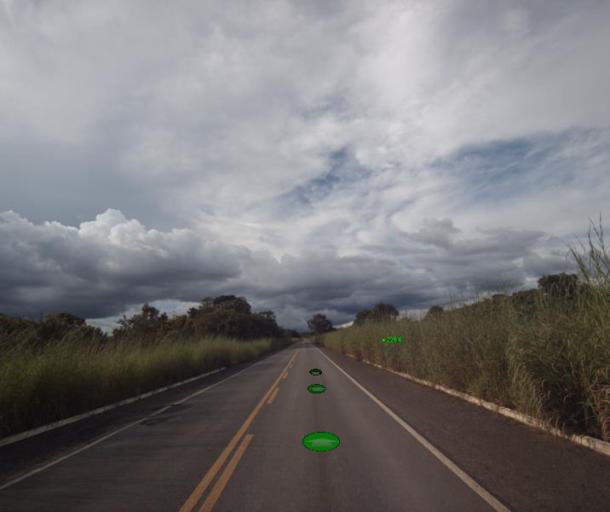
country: BR
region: Goias
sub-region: Niquelandia
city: Niquelandia
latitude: -14.6426
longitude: -48.5901
